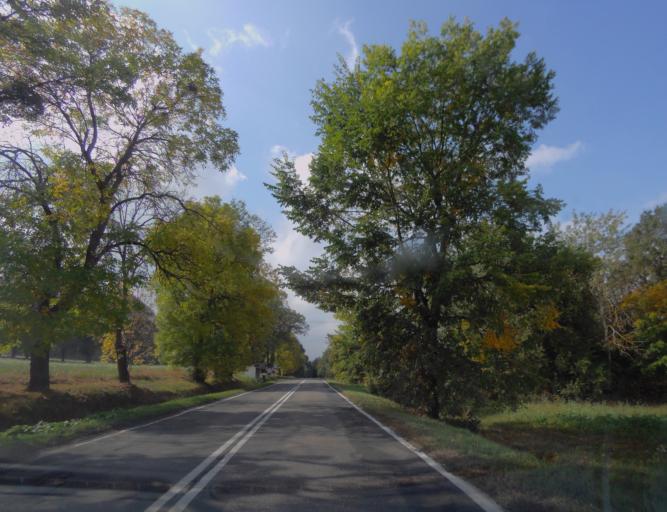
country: PL
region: Lublin Voivodeship
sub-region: Powiat krasnostawski
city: Gorzkow
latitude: 50.9695
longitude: 23.0752
